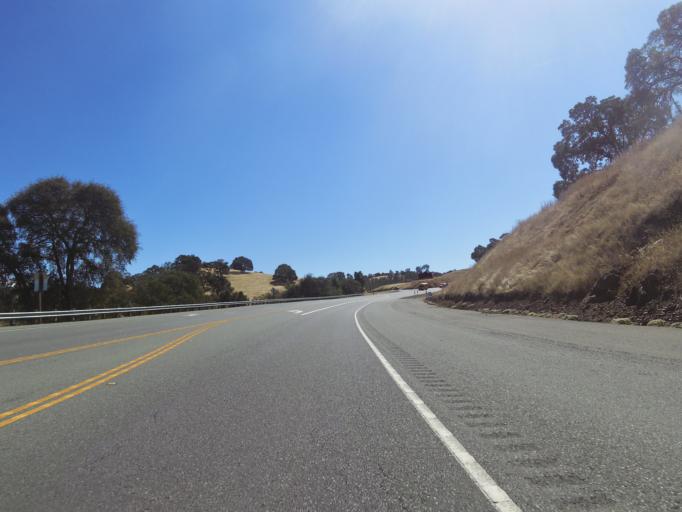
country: US
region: California
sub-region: Amador County
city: Sutter Creek
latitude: 38.4215
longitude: -120.8425
